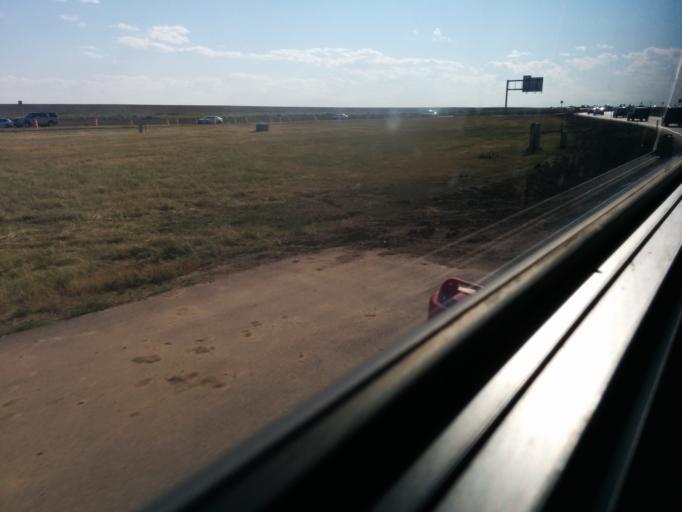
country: US
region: Colorado
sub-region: Adams County
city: Aurora
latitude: 39.8346
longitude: -104.7569
